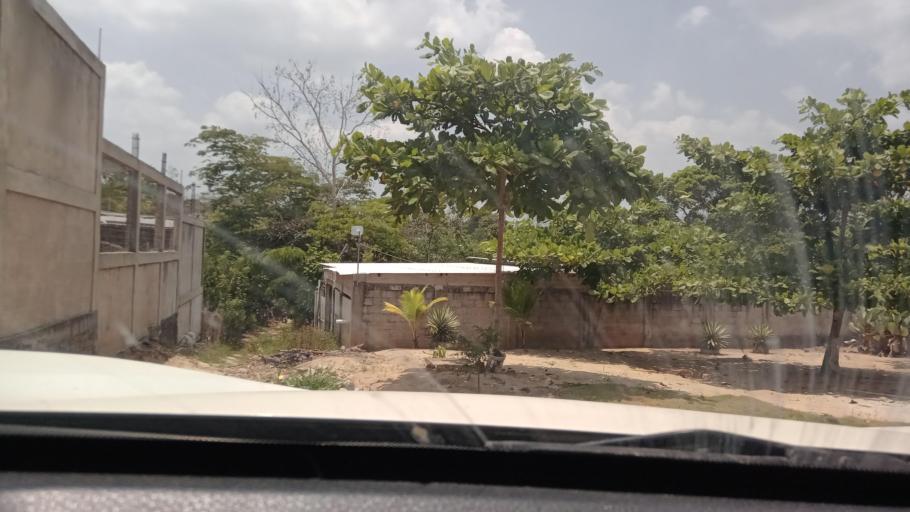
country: MX
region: Veracruz
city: Las Choapas
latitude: 17.9313
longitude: -94.1042
